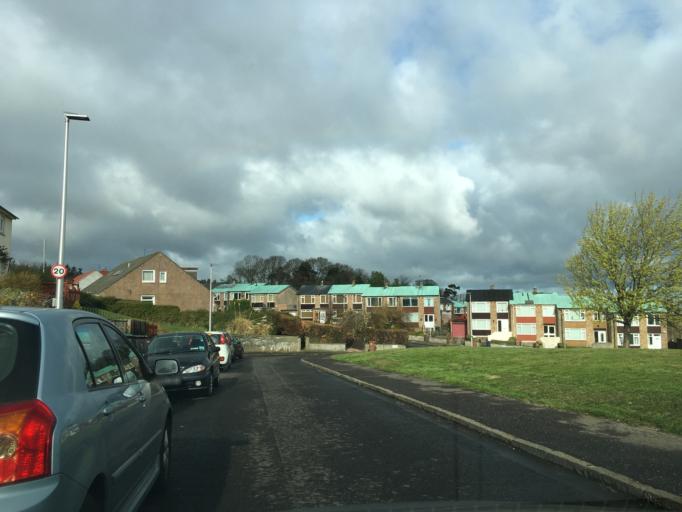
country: GB
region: Scotland
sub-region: Edinburgh
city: Colinton
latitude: 55.9046
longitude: -3.2294
